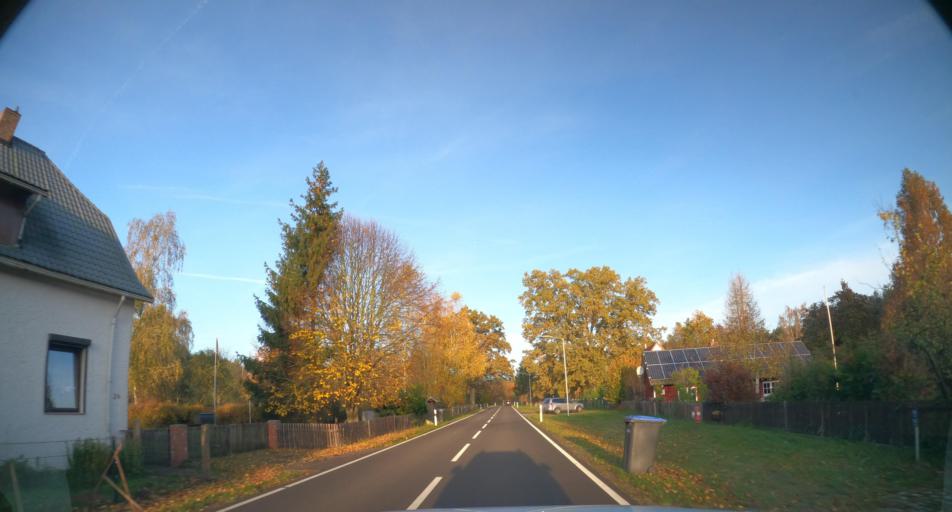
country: DE
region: Mecklenburg-Vorpommern
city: Ahlbeck
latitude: 53.6398
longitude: 14.2084
